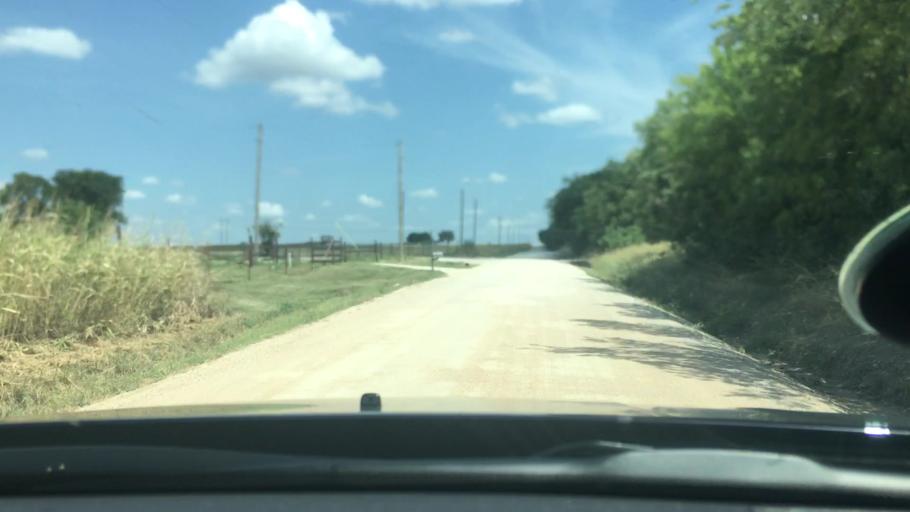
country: US
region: Oklahoma
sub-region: Love County
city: Marietta
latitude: 33.9539
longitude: -97.1869
